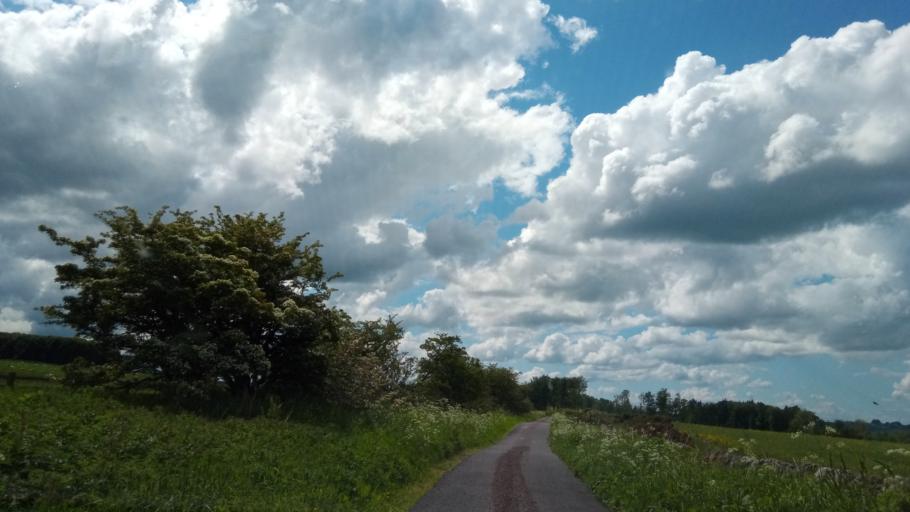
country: GB
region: Scotland
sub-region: The Scottish Borders
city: Coldstream
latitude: 55.5955
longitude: -2.2817
